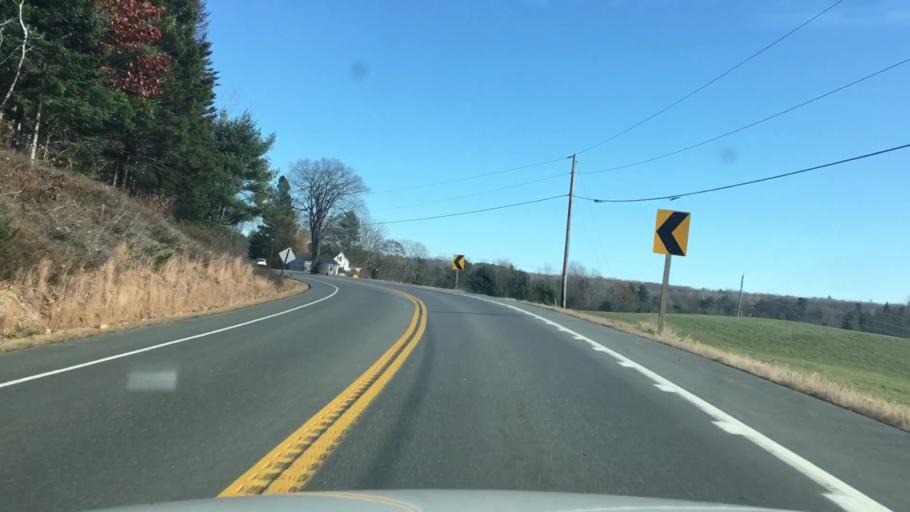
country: US
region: Maine
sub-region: Lincoln County
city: Jefferson
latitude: 44.2511
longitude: -69.4256
